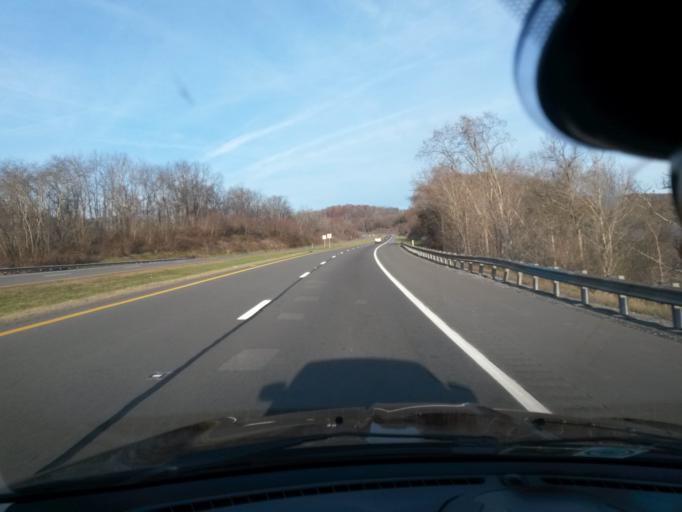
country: US
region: West Virginia
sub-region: Greenbrier County
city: Lewisburg
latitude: 37.8532
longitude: -80.5069
